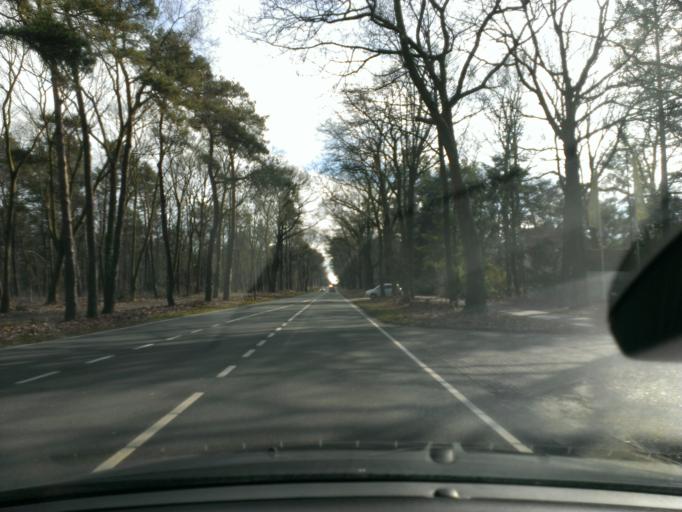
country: NL
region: Gelderland
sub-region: Gemeente Hattem
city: Hattem
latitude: 52.4521
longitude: 6.0042
